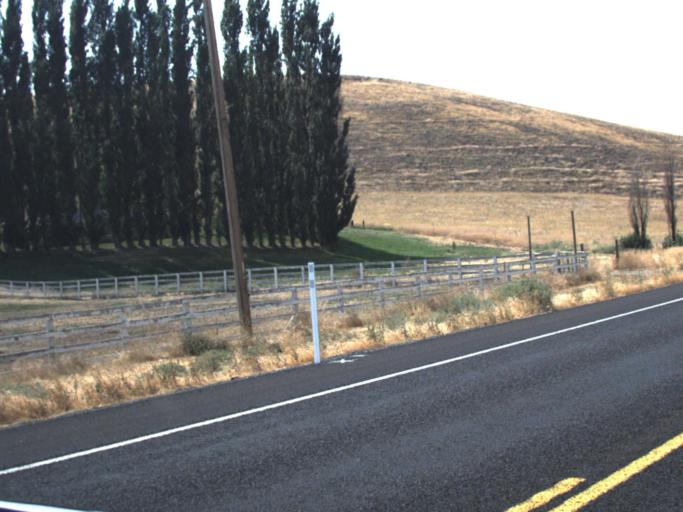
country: US
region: Washington
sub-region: Yakima County
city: Granger
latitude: 46.5050
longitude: -120.0933
